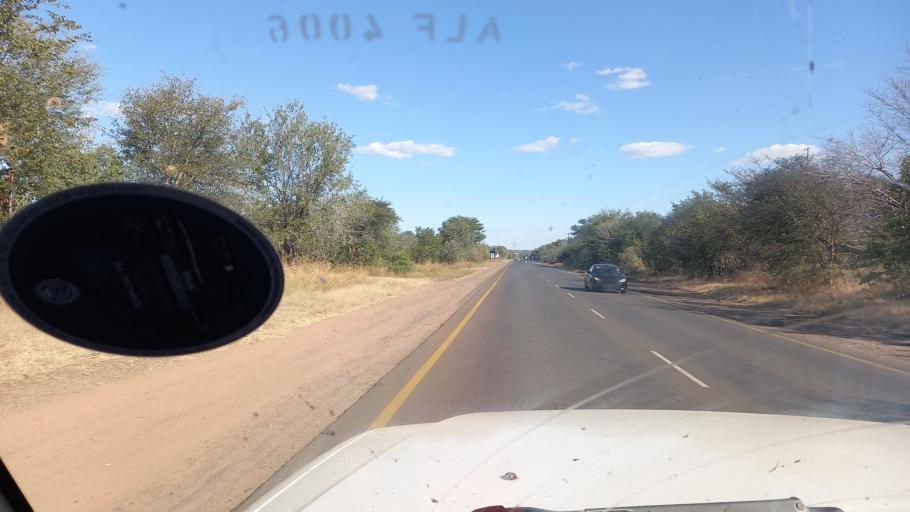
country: ZW
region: Matabeleland North
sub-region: Hwange District
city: Victoria Falls
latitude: -17.9173
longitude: 25.8666
